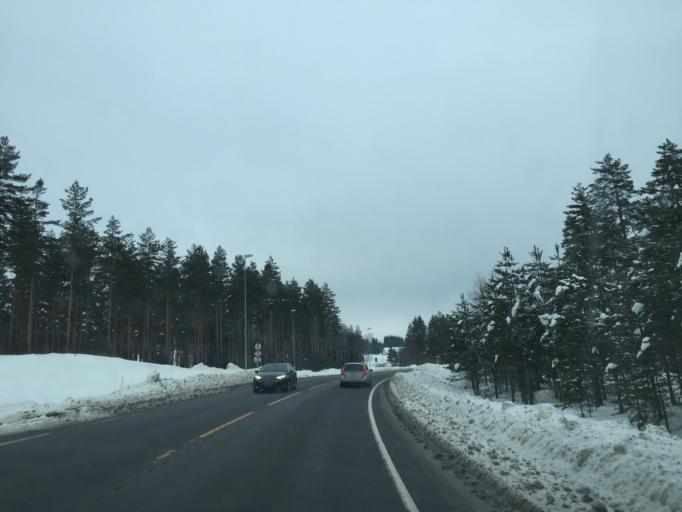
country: NO
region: Hedmark
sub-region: Elverum
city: Elverum
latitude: 60.9048
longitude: 11.6031
